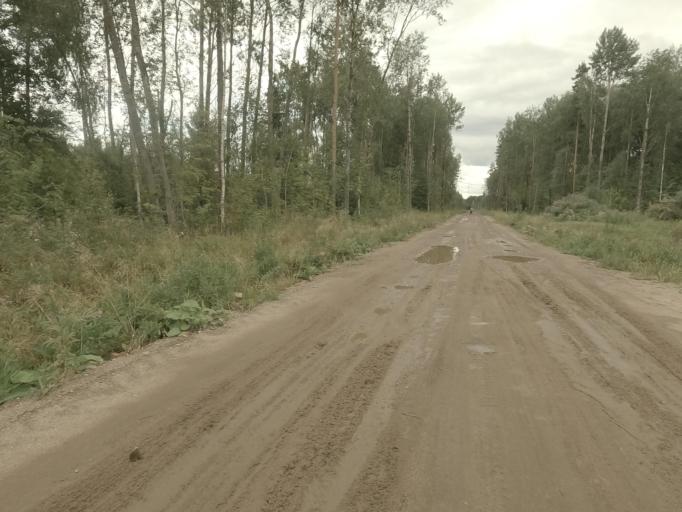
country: RU
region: Leningrad
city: Kirovsk
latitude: 59.9044
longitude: 31.0036
